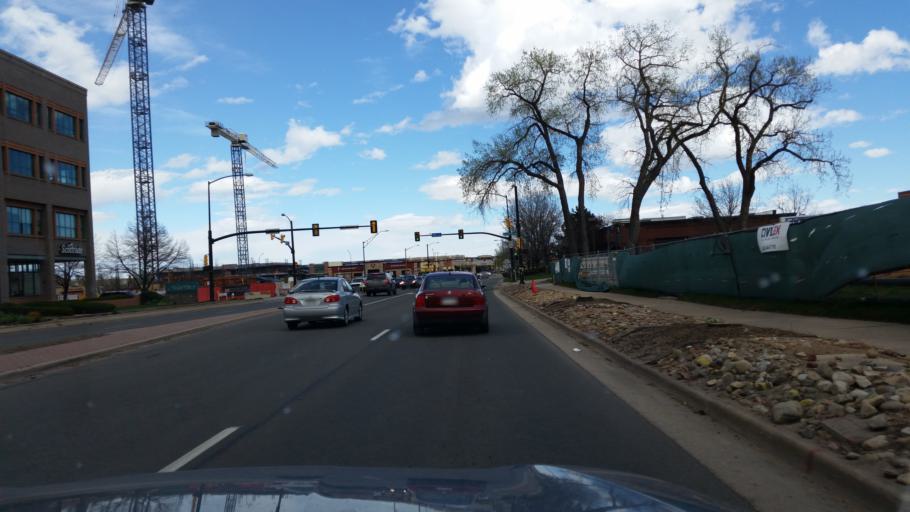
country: US
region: Colorado
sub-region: Boulder County
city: Boulder
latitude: 40.0174
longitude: -105.2615
